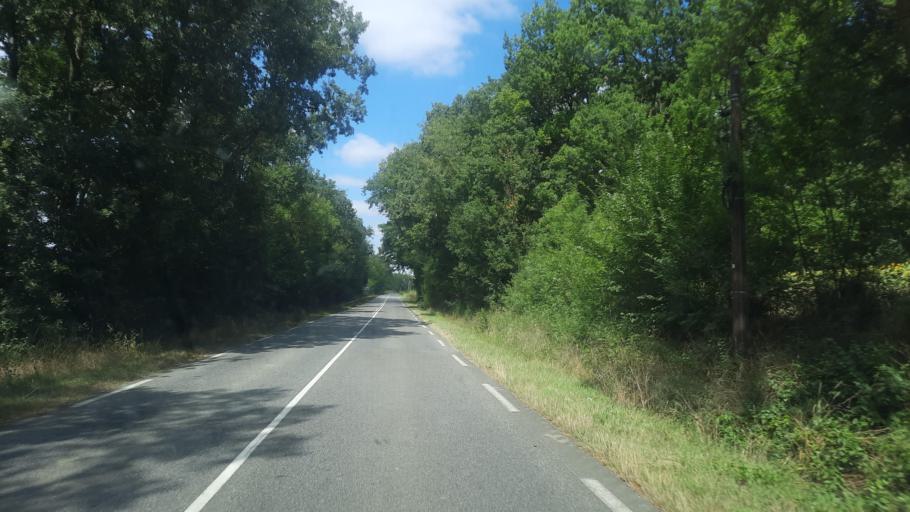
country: FR
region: Midi-Pyrenees
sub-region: Departement du Gers
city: Samatan
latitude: 43.4990
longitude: 0.9705
